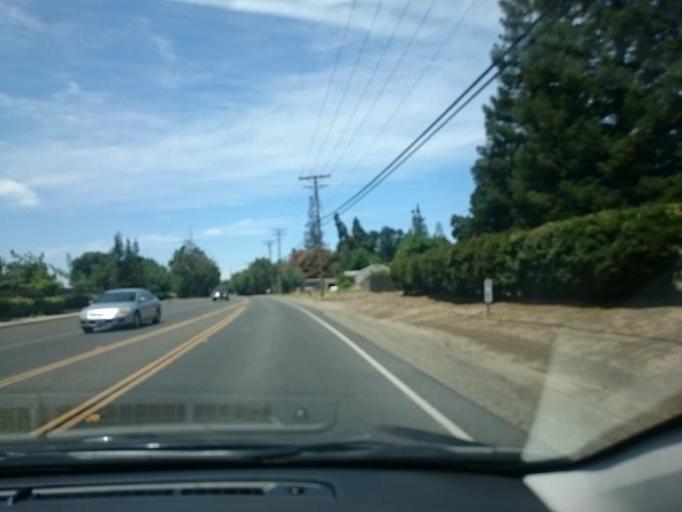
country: US
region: California
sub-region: Stanislaus County
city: Waterford
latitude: 37.6398
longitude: -120.7502
